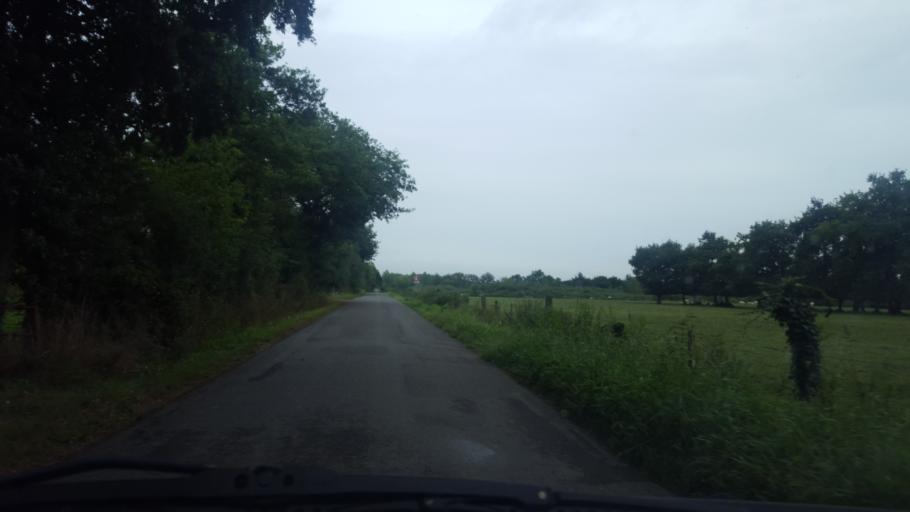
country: FR
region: Pays de la Loire
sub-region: Departement de la Loire-Atlantique
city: Saint-Philbert-de-Grand-Lieu
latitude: 47.0440
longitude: -1.6736
